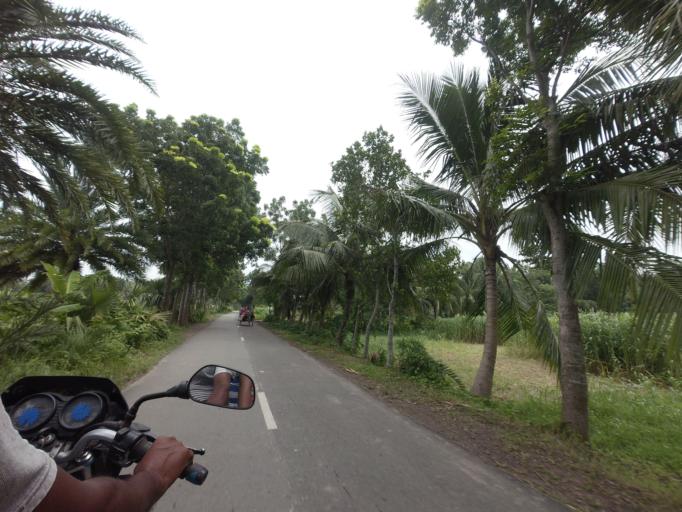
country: BD
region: Khulna
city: Kalia
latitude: 23.1063
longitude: 89.6471
